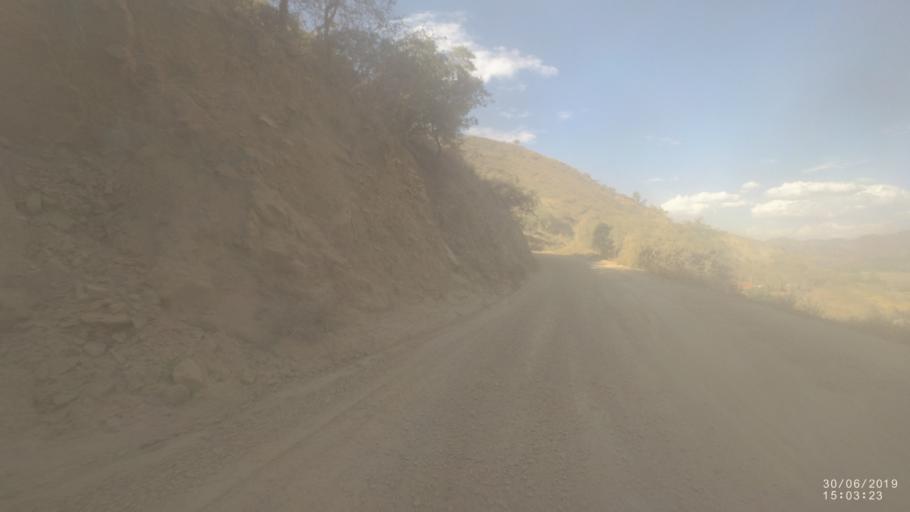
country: BO
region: Cochabamba
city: Irpa Irpa
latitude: -17.7315
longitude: -66.3273
